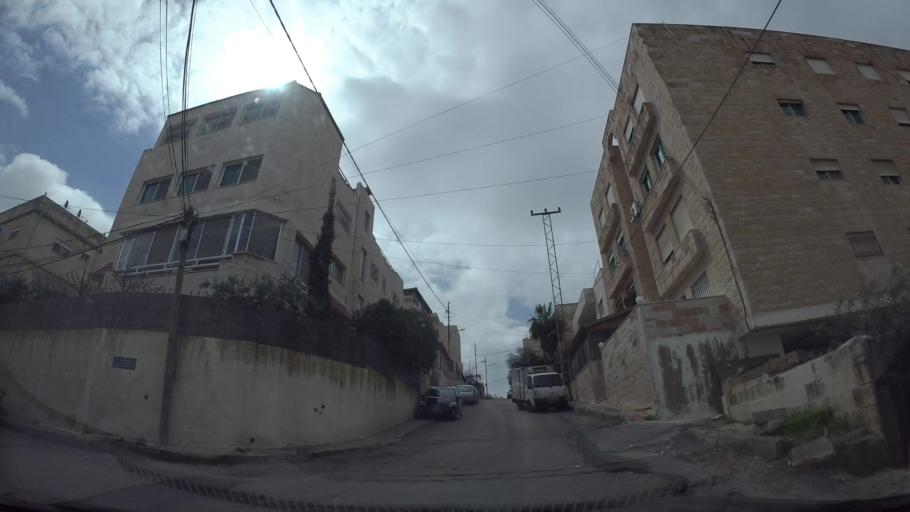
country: JO
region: Amman
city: Wadi as Sir
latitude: 31.9545
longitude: 35.8303
